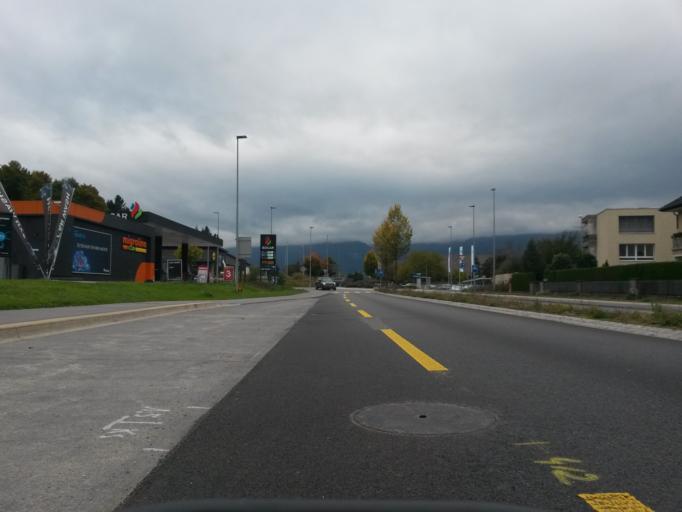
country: CH
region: Solothurn
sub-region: Bezirk Wasseramt
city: Biberist
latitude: 47.1898
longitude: 7.5539
